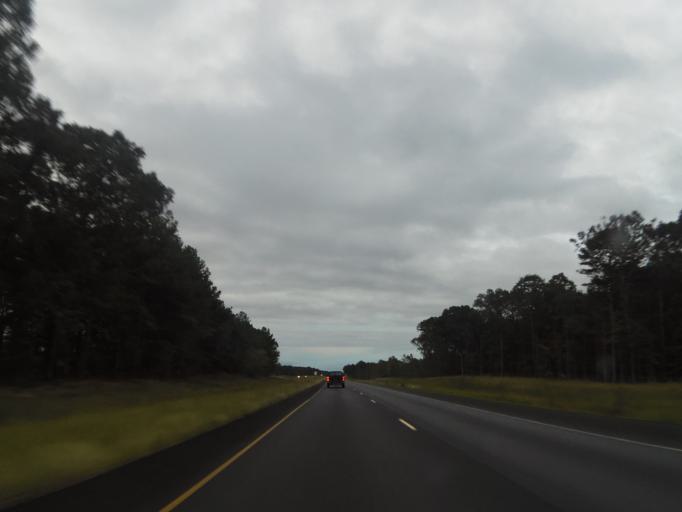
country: US
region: Alabama
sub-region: Saint Clair County
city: Steele
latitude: 33.9586
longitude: -86.1343
